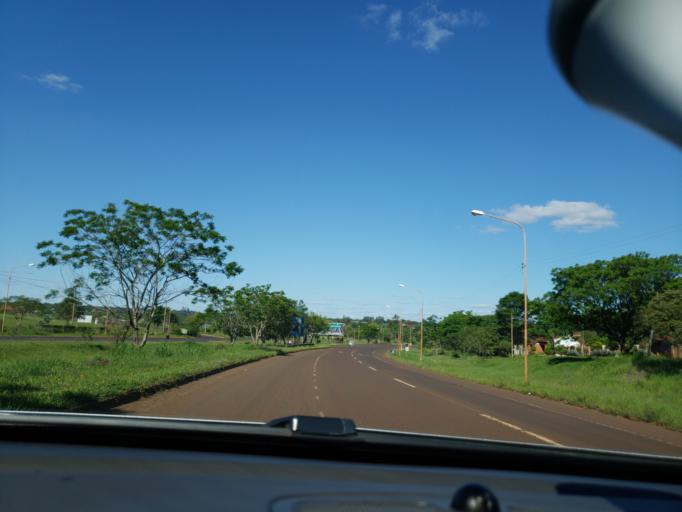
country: AR
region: Misiones
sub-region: Departamento de Capital
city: Posadas
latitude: -27.3988
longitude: -55.9619
